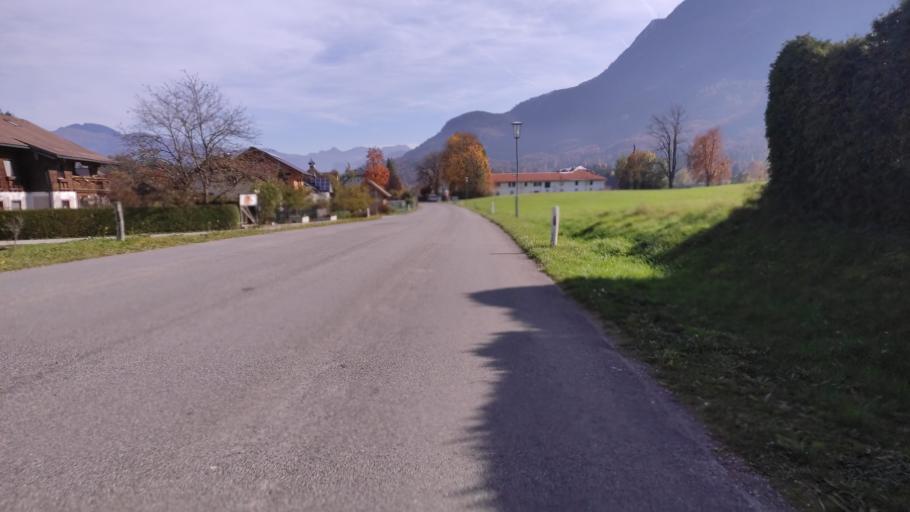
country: AT
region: Salzburg
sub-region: Politischer Bezirk Salzburg-Umgebung
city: Strobl
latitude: 47.7157
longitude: 13.5333
